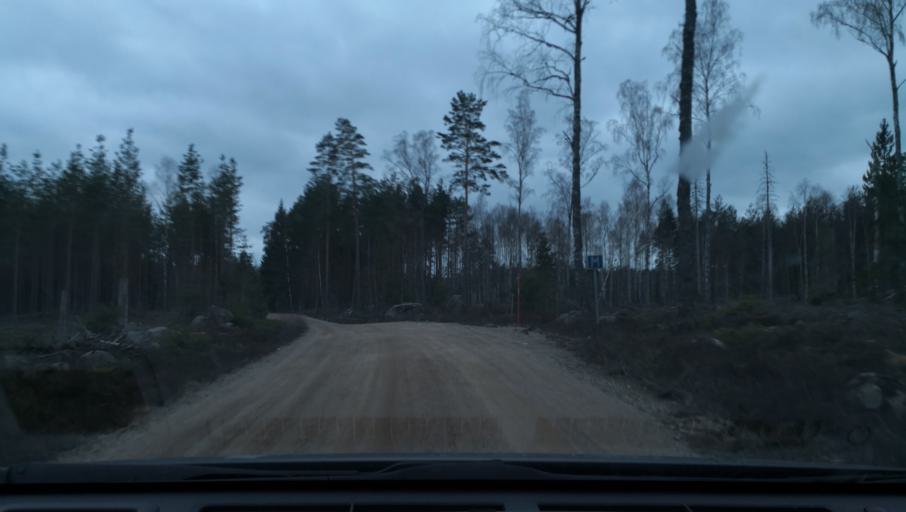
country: SE
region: OErebro
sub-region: Lindesbergs Kommun
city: Fellingsbro
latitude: 59.5880
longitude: 15.5755
